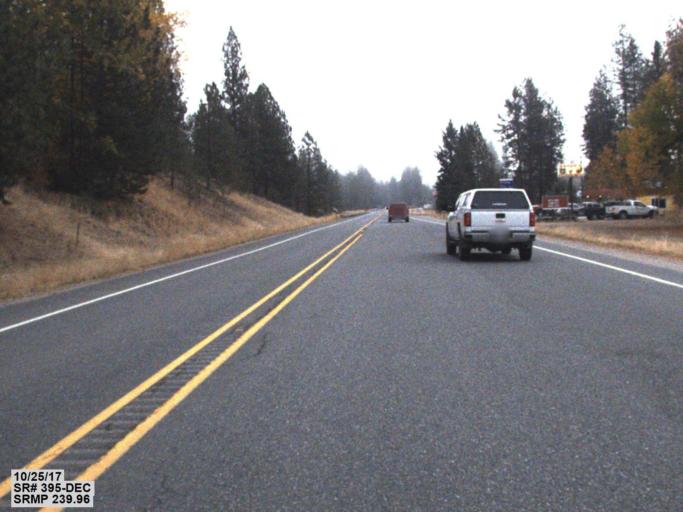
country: US
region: Washington
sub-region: Stevens County
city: Kettle Falls
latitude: 48.6105
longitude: -118.0909
